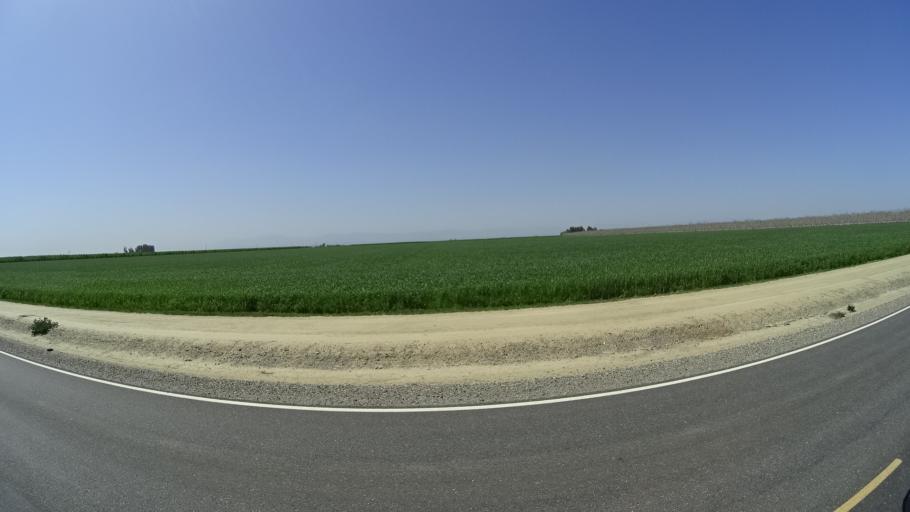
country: US
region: California
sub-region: Glenn County
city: Willows
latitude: 39.6062
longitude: -122.1379
